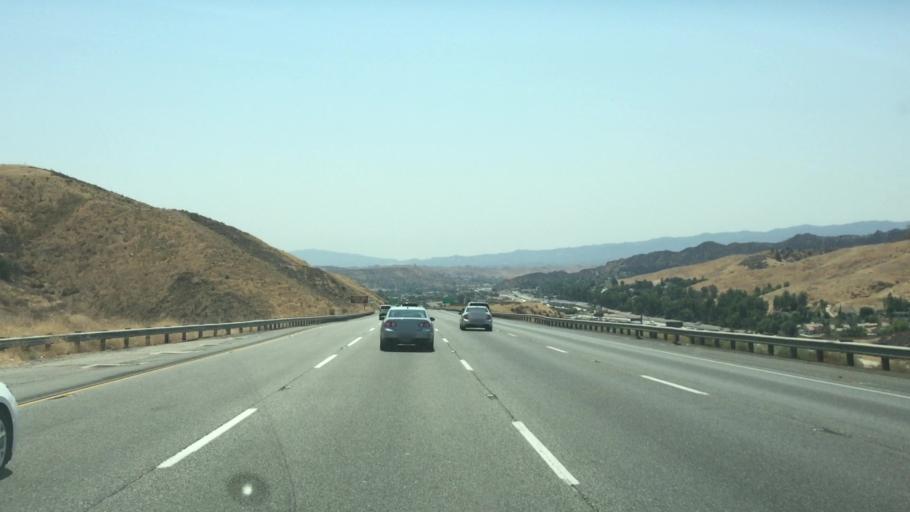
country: US
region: California
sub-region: Los Angeles County
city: Castaic
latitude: 34.5151
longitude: -118.6343
